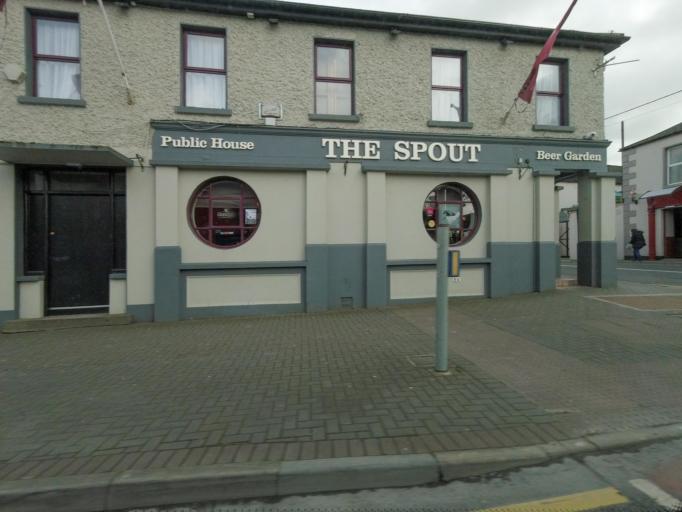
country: IE
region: Leinster
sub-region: Kildare
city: Kilcullen
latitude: 53.1305
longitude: -6.7455
